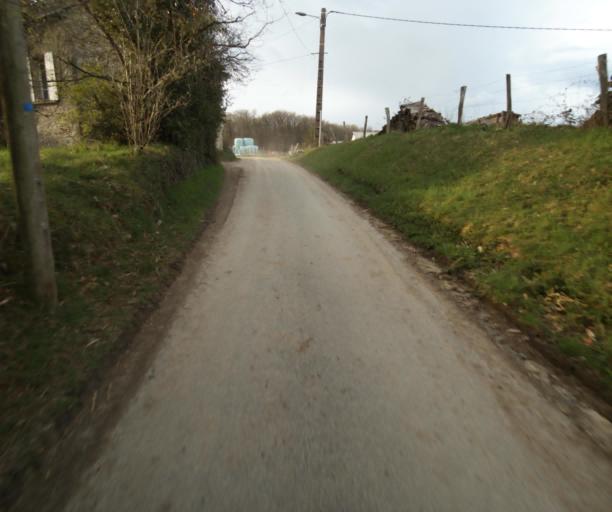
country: FR
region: Limousin
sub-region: Departement de la Correze
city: Argentat
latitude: 45.2287
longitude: 1.9503
